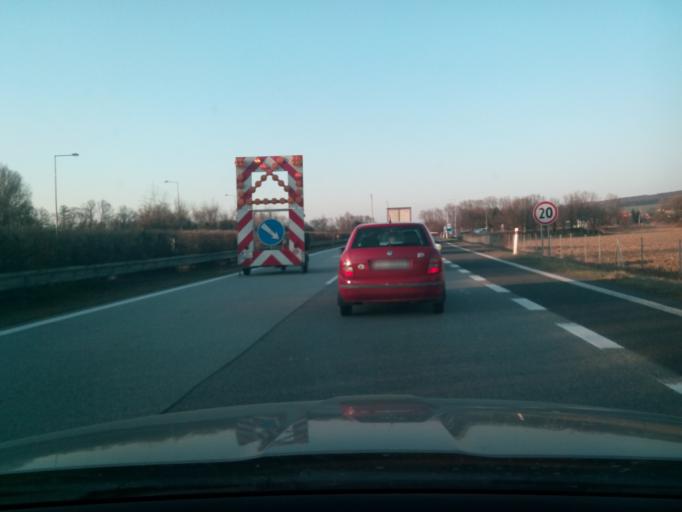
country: SK
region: Presovsky
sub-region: Okres Presov
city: Presov
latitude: 48.9132
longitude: 21.2517
